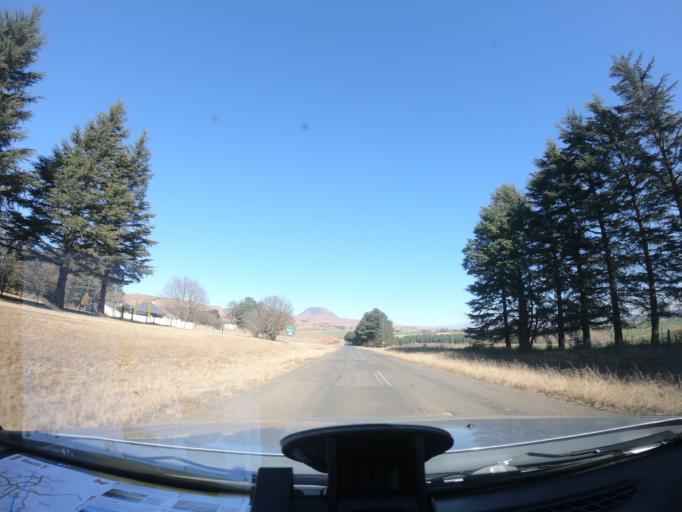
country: ZA
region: KwaZulu-Natal
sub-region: uMgungundlovu District Municipality
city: Mooirivier
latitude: -29.3288
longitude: 29.8240
